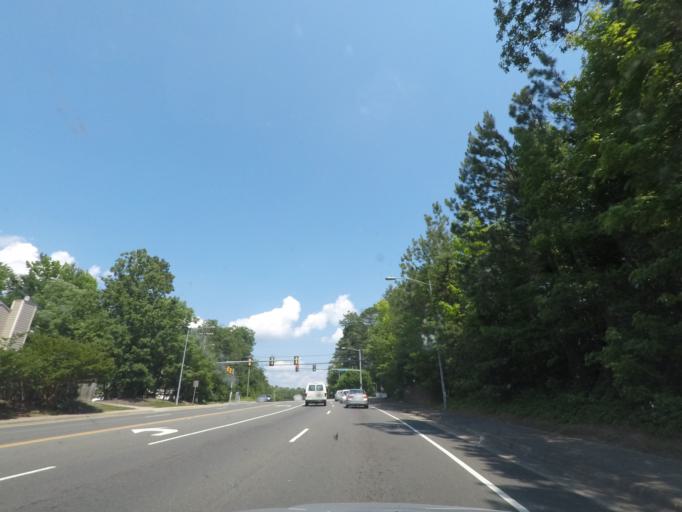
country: US
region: North Carolina
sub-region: Durham County
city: Durham
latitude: 35.9585
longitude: -78.9484
